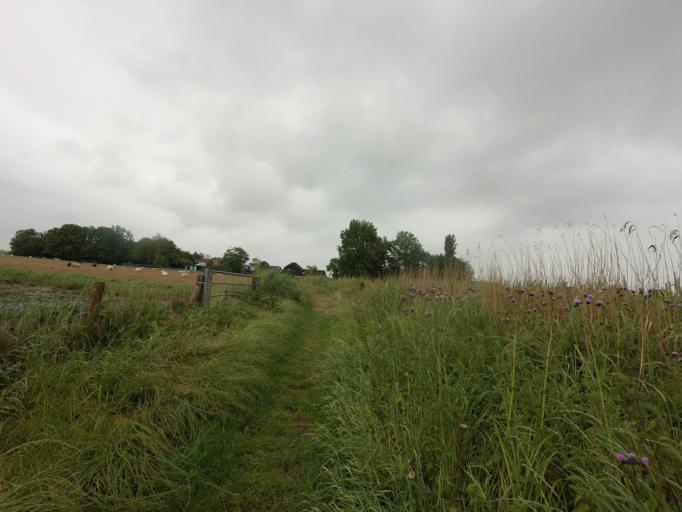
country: NL
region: North Holland
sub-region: Gemeente Schagen
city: Schagen
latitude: 52.7653
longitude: 4.8014
